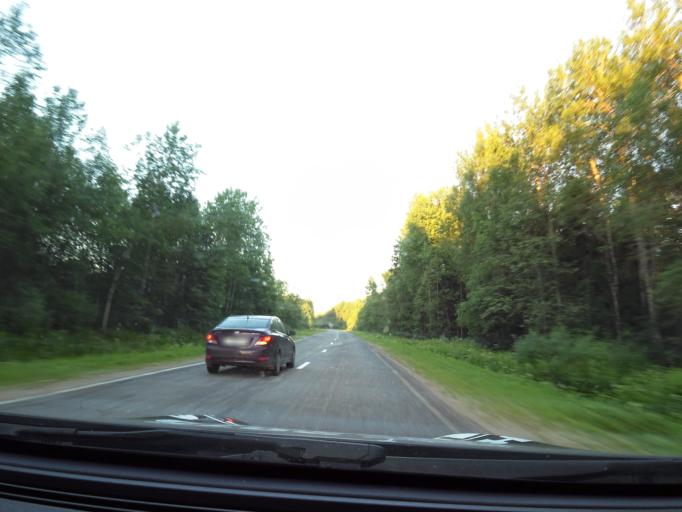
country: RU
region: Jaroslavl
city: Prechistoye
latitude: 58.3964
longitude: 40.4069
